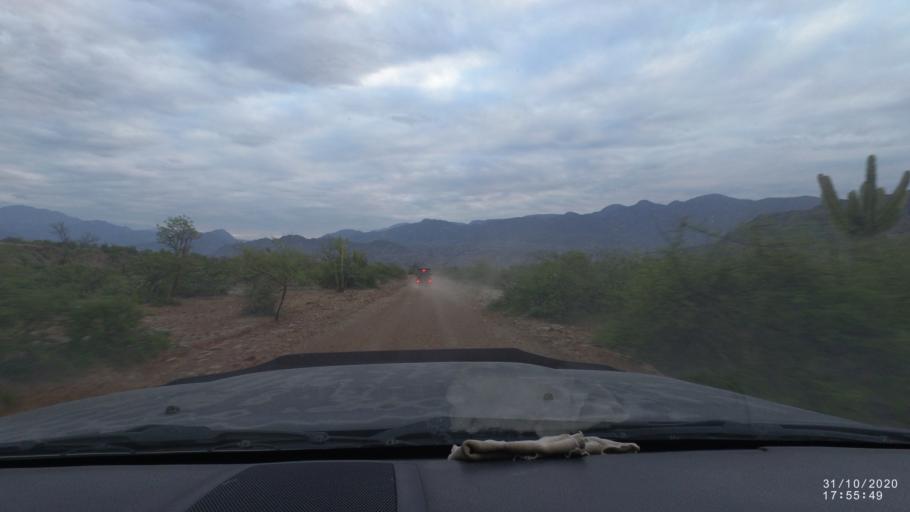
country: BO
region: Chuquisaca
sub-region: Provincia Zudanez
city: Mojocoya
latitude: -18.6468
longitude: -64.5286
